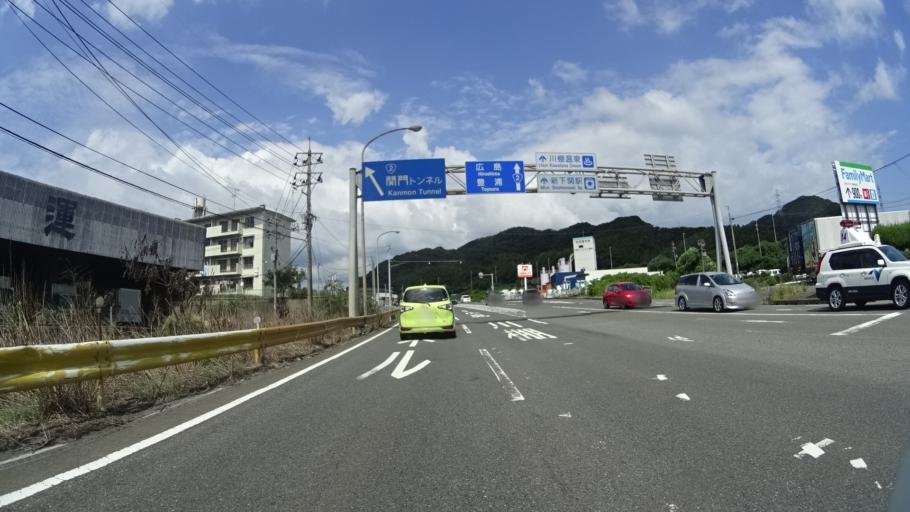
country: JP
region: Yamaguchi
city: Shimonoseki
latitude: 33.9802
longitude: 130.9507
